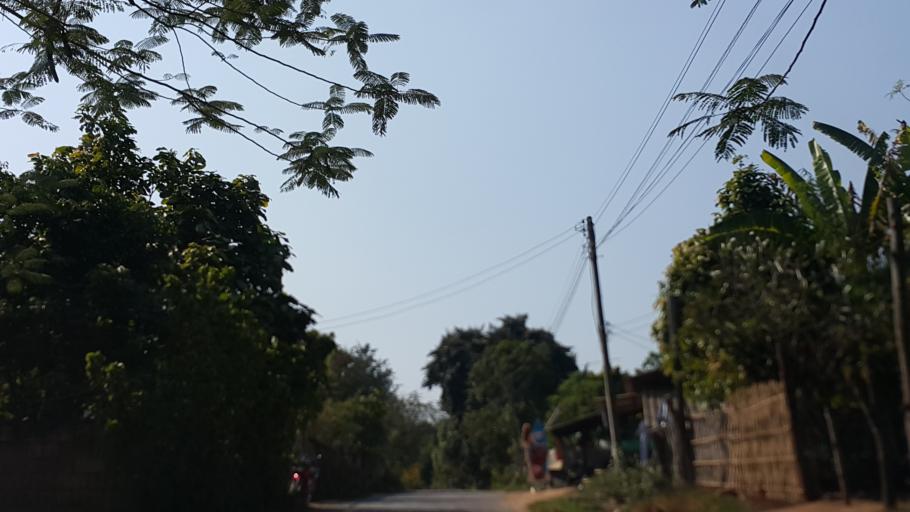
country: TH
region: Chiang Mai
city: Mae Taeng
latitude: 19.2178
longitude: 98.8585
